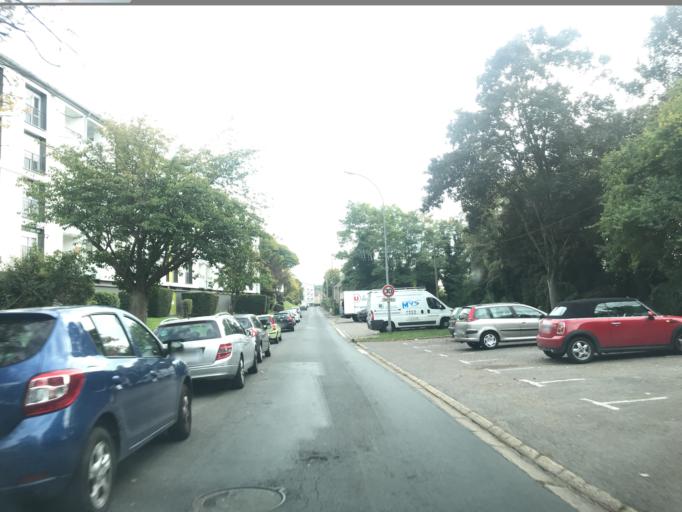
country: FR
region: Haute-Normandie
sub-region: Departement de la Seine-Maritime
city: Deville-les-Rouen
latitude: 49.4643
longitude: 1.0553
